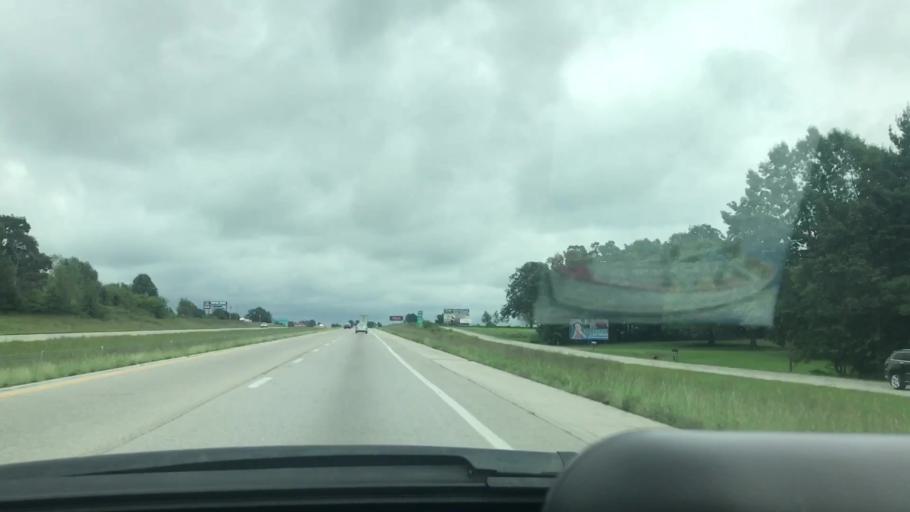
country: US
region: Missouri
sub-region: Lawrence County
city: Mount Vernon
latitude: 37.0857
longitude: -93.8332
